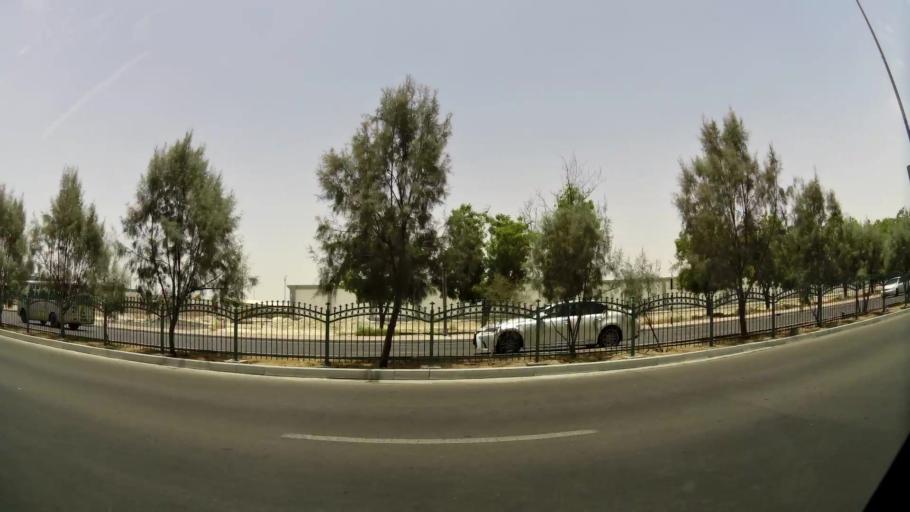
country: AE
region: Abu Dhabi
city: Al Ain
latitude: 24.2053
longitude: 55.7523
